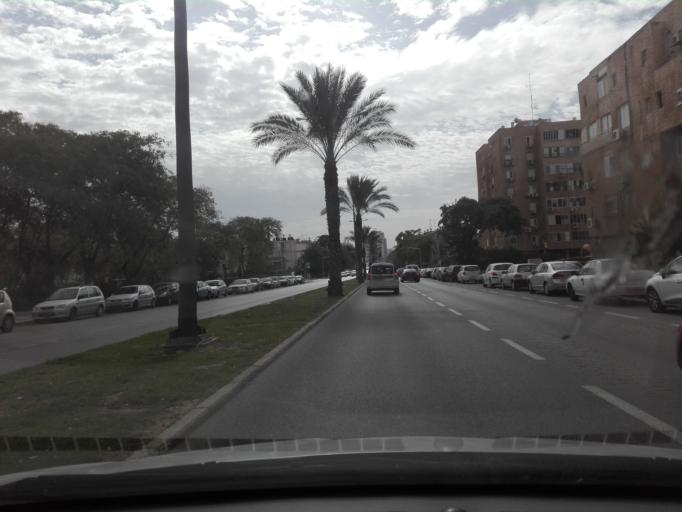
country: IL
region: Southern District
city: Beersheba
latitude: 31.2674
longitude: 34.7981
